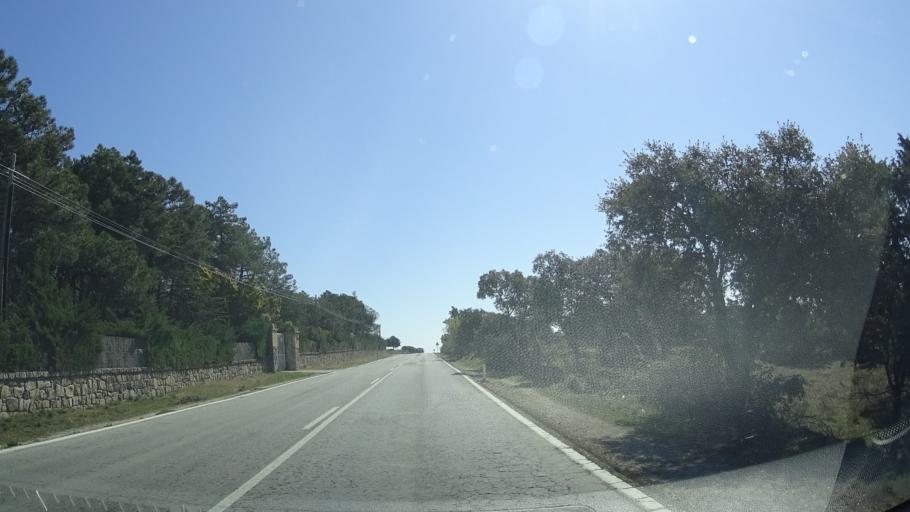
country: ES
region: Madrid
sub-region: Provincia de Madrid
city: Hoyo de Manzanares
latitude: 40.6222
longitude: -3.8942
